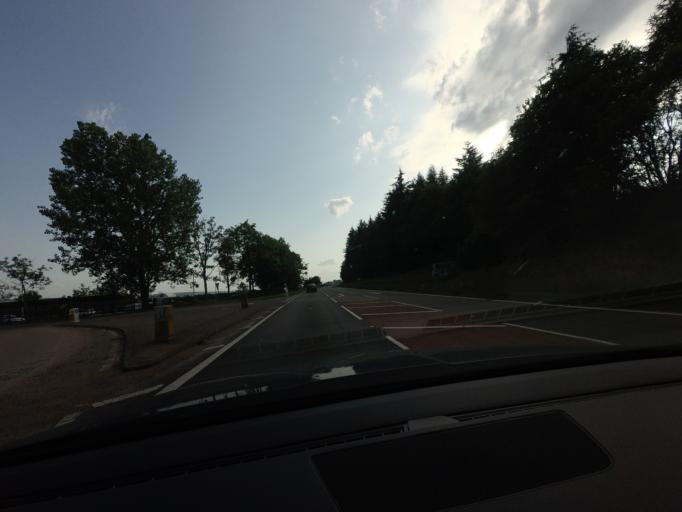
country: GB
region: Scotland
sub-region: Highland
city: Evanton
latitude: 57.6406
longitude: -4.3492
